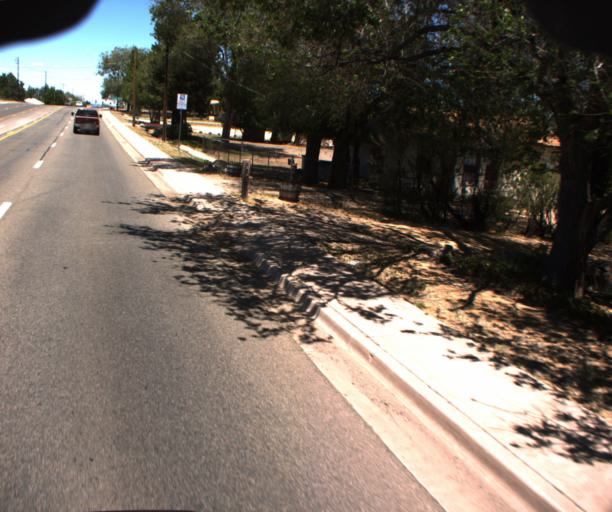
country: US
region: Arizona
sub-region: Yavapai County
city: Chino Valley
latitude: 34.7426
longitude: -112.4545
